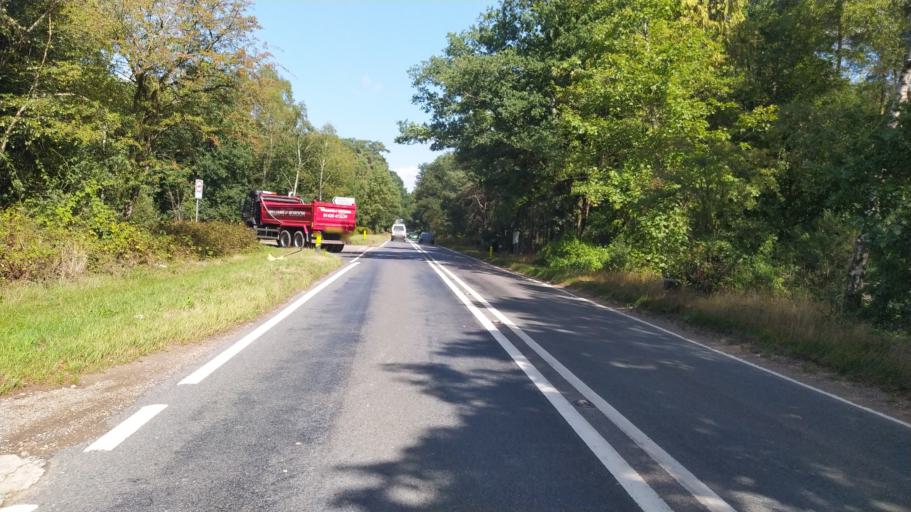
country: GB
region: England
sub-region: Hampshire
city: Bordon
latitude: 51.0848
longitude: -0.8789
